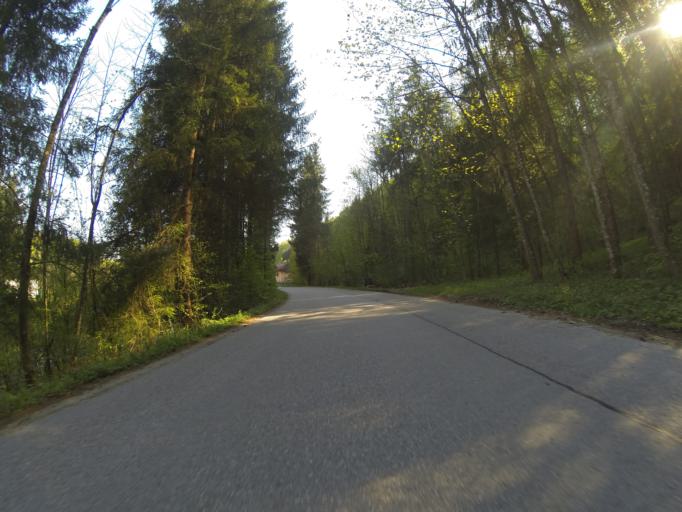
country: AT
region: Upper Austria
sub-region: Politischer Bezirk Gmunden
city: Altmunster
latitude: 47.9430
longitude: 13.7498
